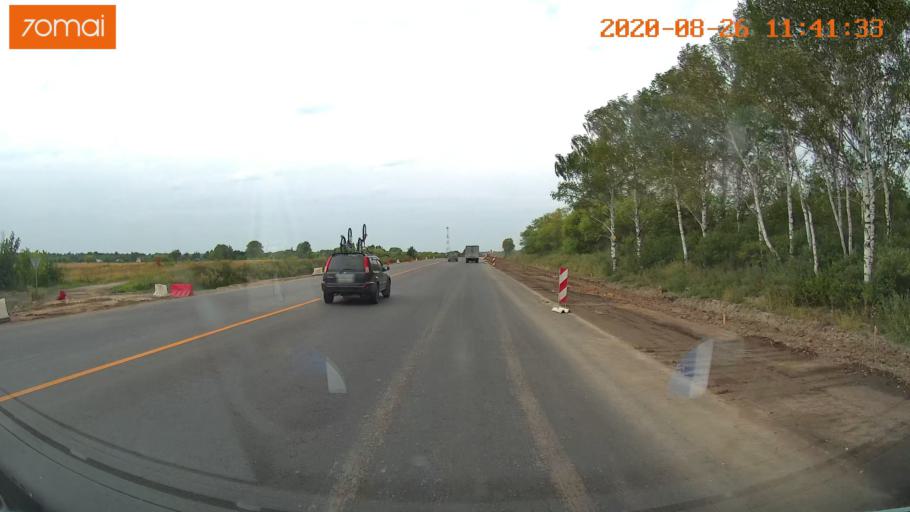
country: RU
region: Rjazan
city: Shilovo
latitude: 54.2955
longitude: 40.7094
